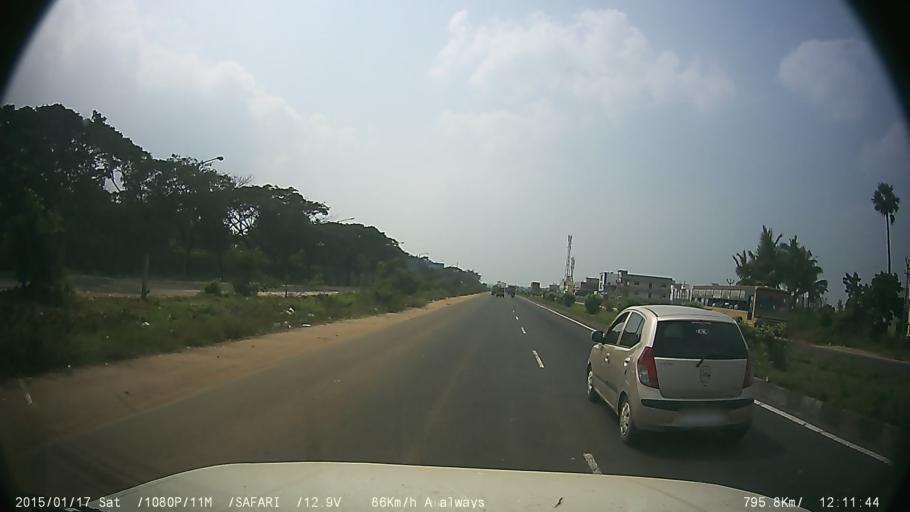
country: IN
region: Tamil Nadu
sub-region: Kancheepuram
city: Sriperumbudur
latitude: 12.9367
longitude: 79.9120
